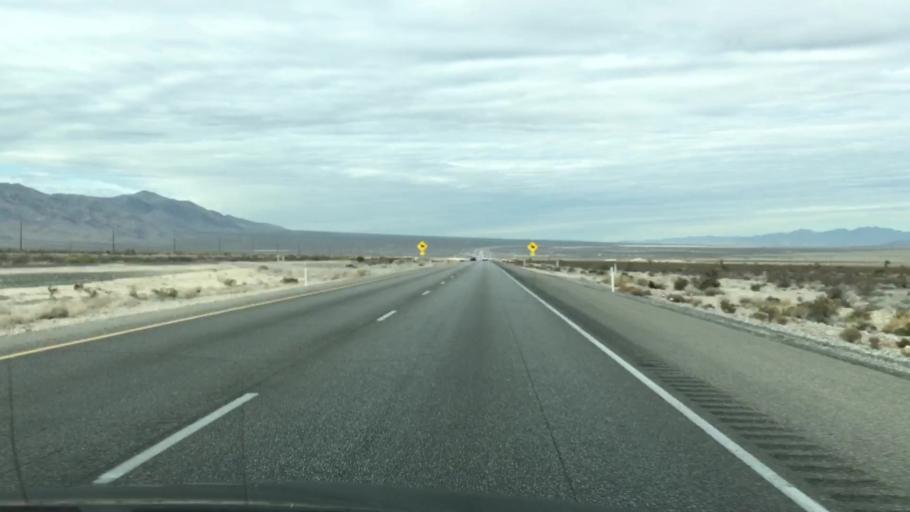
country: US
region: Nevada
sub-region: Clark County
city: Summerlin South
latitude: 36.3870
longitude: -115.3809
